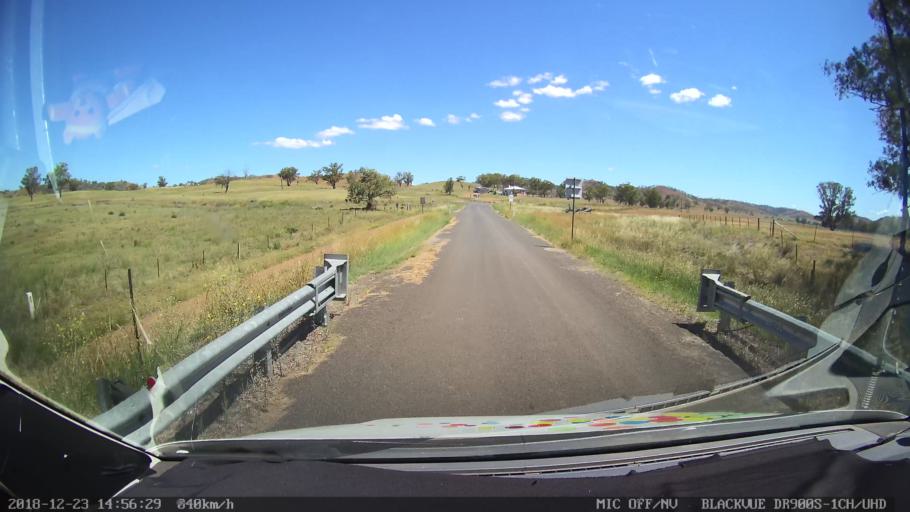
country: AU
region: New South Wales
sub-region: Tamworth Municipality
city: Manilla
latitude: -30.7041
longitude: 150.8294
